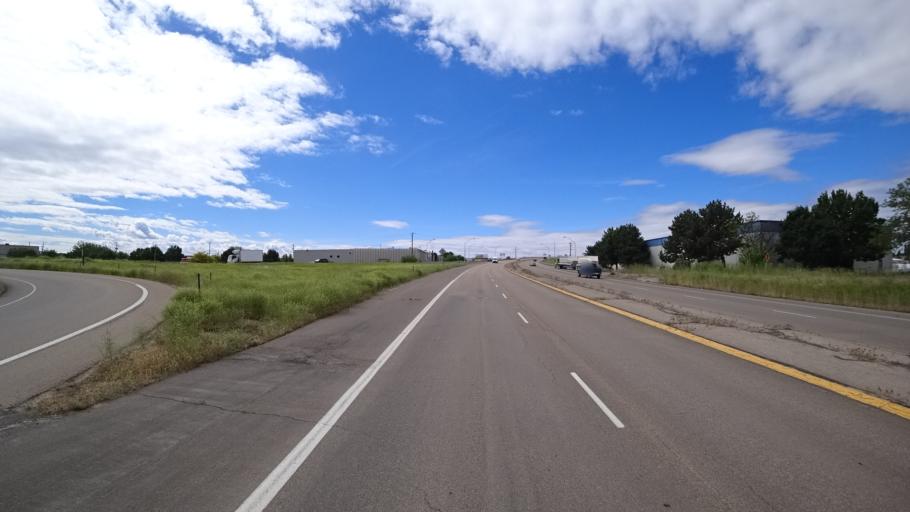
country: US
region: Idaho
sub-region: Ada County
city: Boise
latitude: 43.5728
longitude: -116.1935
